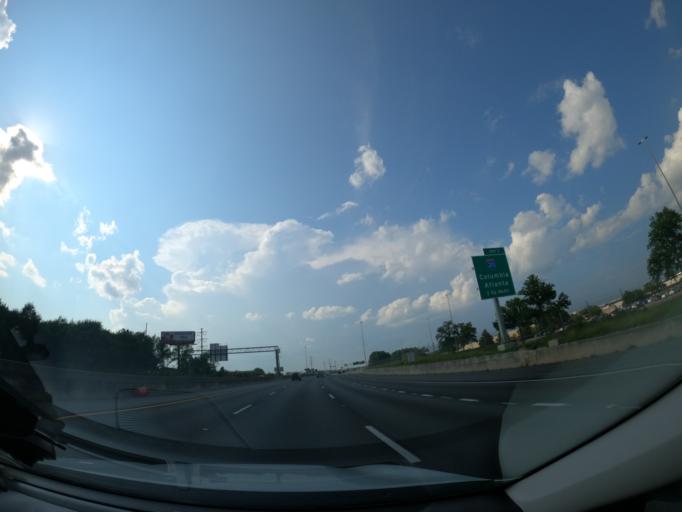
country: US
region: Georgia
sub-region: Columbia County
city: Martinez
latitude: 33.4613
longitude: -82.0807
